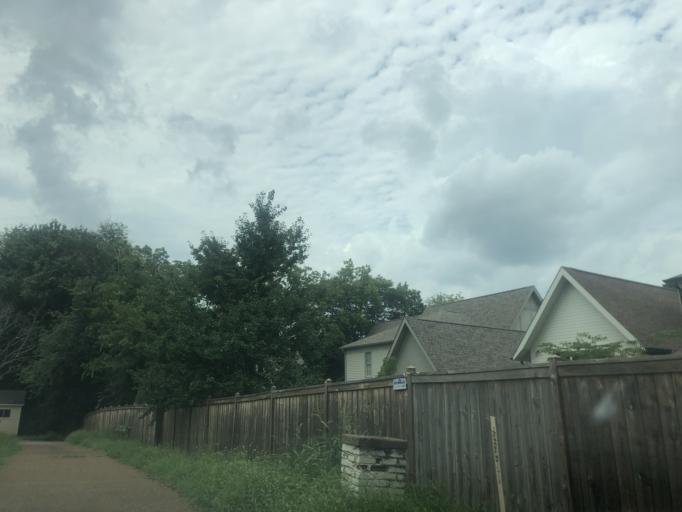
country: US
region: Tennessee
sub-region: Davidson County
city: Oak Hill
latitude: 36.0962
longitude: -86.7987
